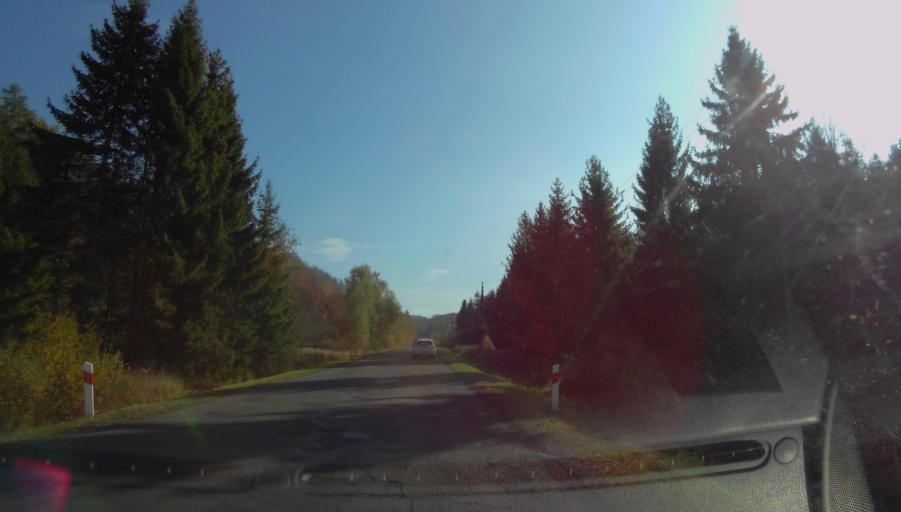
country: PL
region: Subcarpathian Voivodeship
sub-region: Powiat leski
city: Cisna
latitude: 49.2203
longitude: 22.2057
